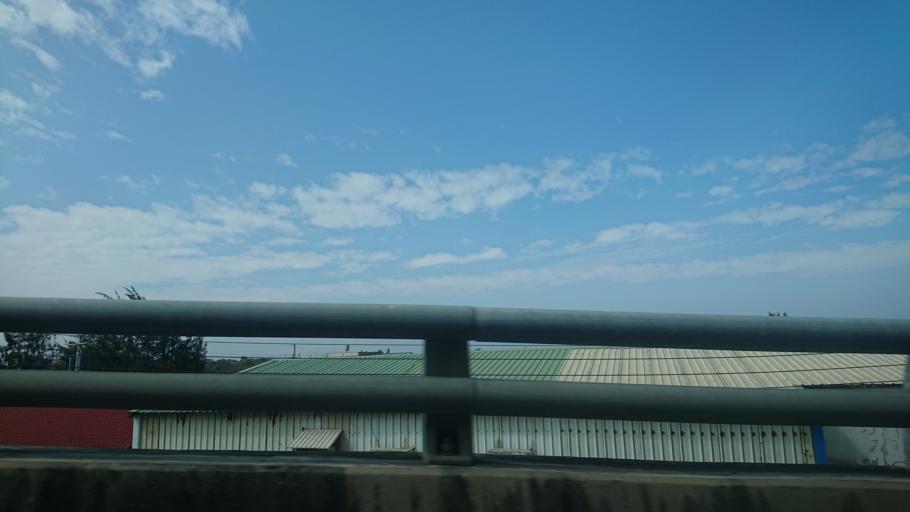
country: TW
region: Taiwan
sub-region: Yunlin
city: Douliu
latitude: 23.8591
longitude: 120.2957
